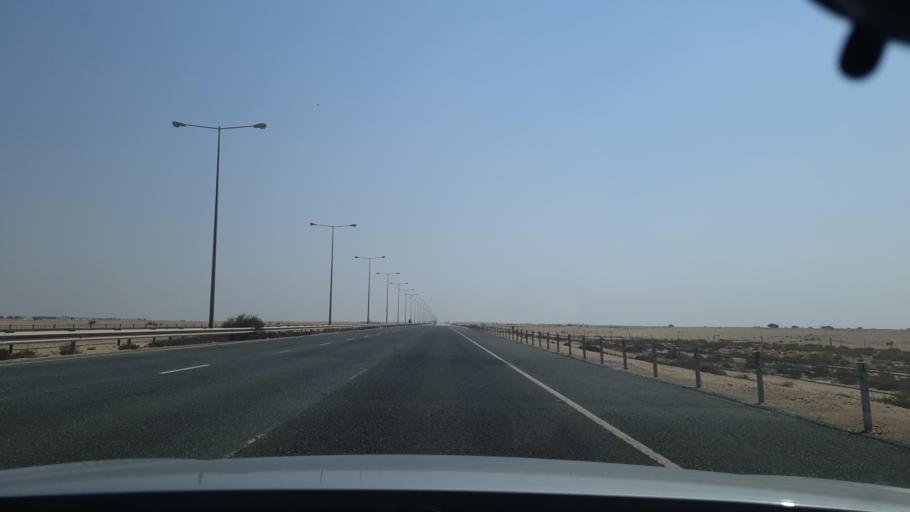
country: QA
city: Al Ghuwayriyah
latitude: 25.8083
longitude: 51.3761
